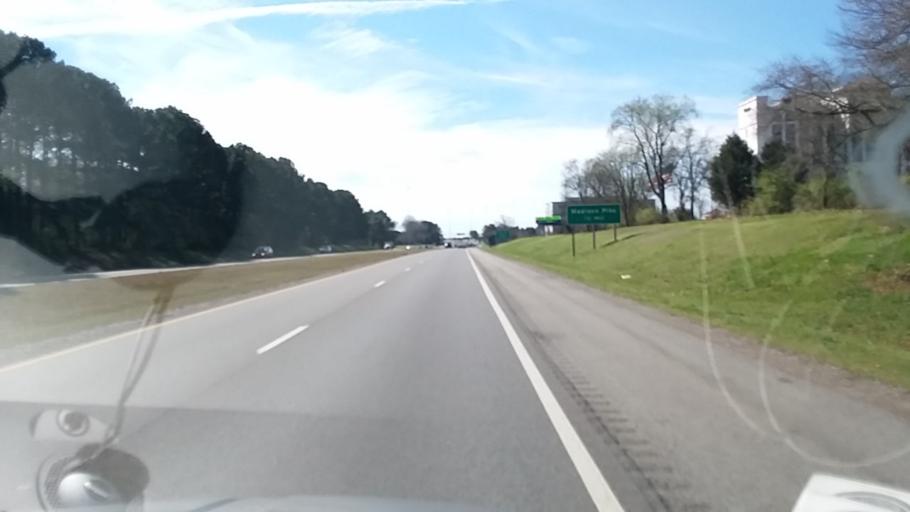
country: US
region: Alabama
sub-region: Madison County
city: Redstone Arsenal
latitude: 34.7207
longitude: -86.6707
